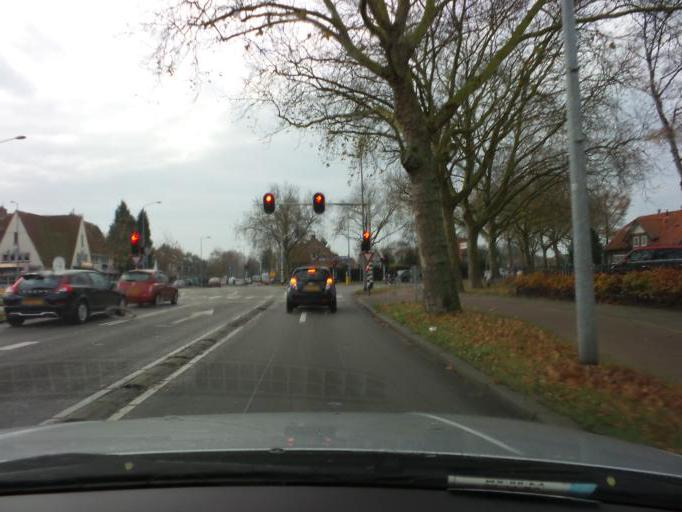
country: NL
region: North Holland
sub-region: Gemeente Hilversum
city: Hilversum
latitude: 52.2368
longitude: 5.1949
